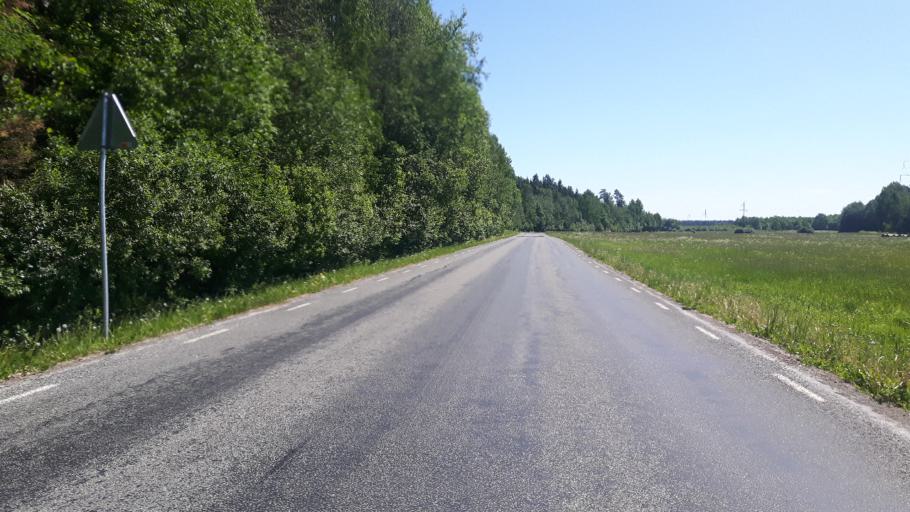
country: EE
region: Raplamaa
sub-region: Kohila vald
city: Kohila
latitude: 59.2083
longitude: 24.6857
